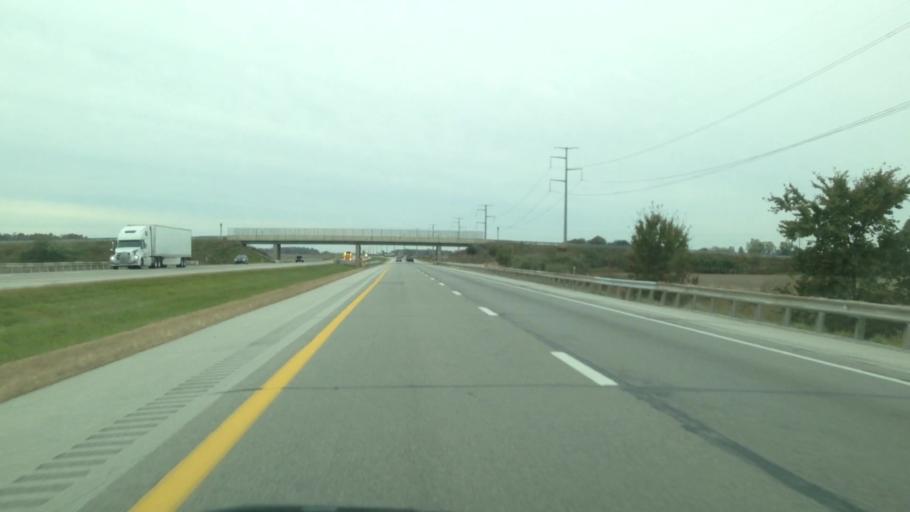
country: US
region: Ohio
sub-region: Fulton County
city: Swanton
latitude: 41.5999
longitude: -83.9378
